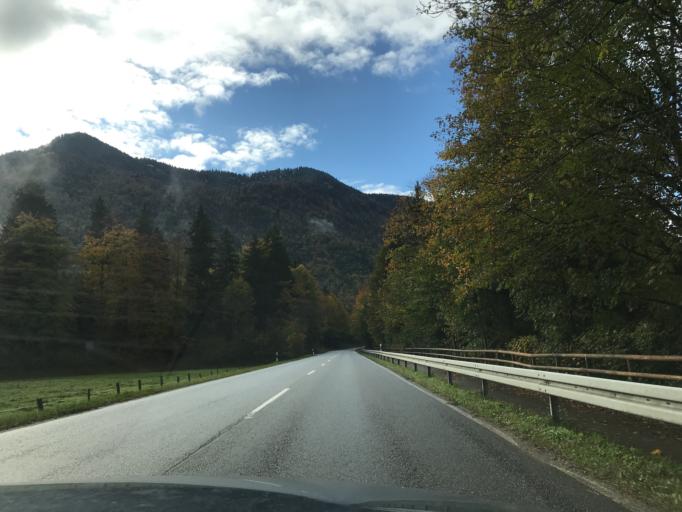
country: DE
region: Bavaria
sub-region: Upper Bavaria
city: Lenggries
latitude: 47.6269
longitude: 11.5948
